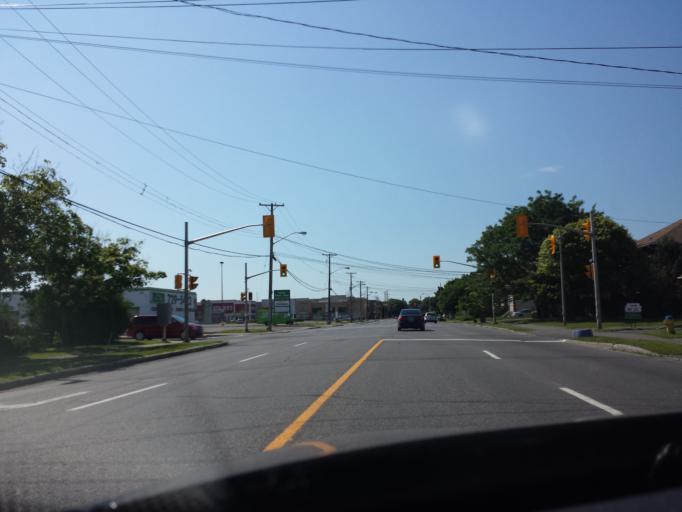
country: CA
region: Ontario
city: Bells Corners
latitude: 45.3723
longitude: -75.7719
